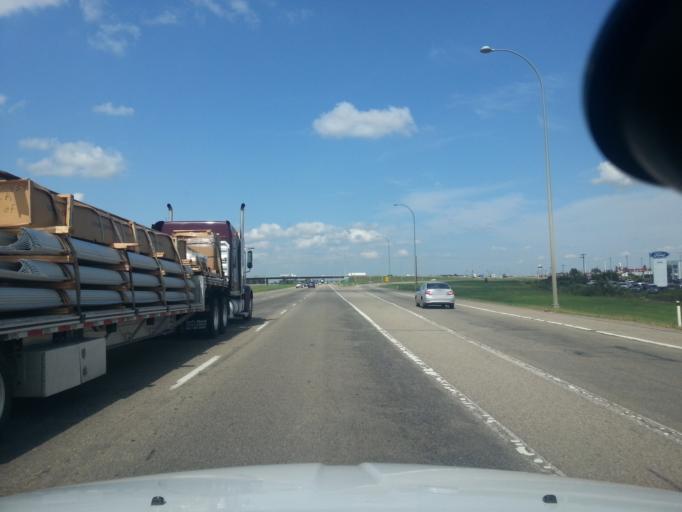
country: CA
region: Alberta
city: Leduc
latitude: 53.3319
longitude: -113.5479
